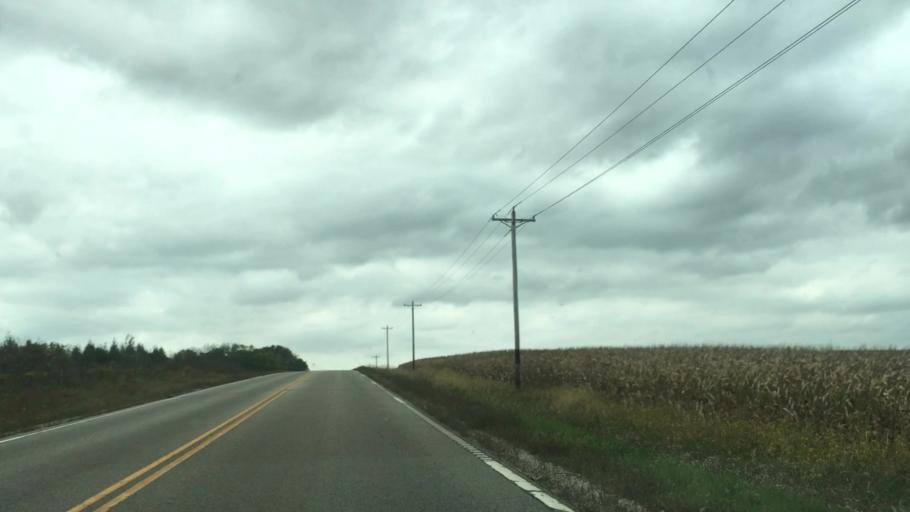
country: US
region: Minnesota
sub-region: Fillmore County
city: Preston
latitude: 43.7315
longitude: -92.0381
